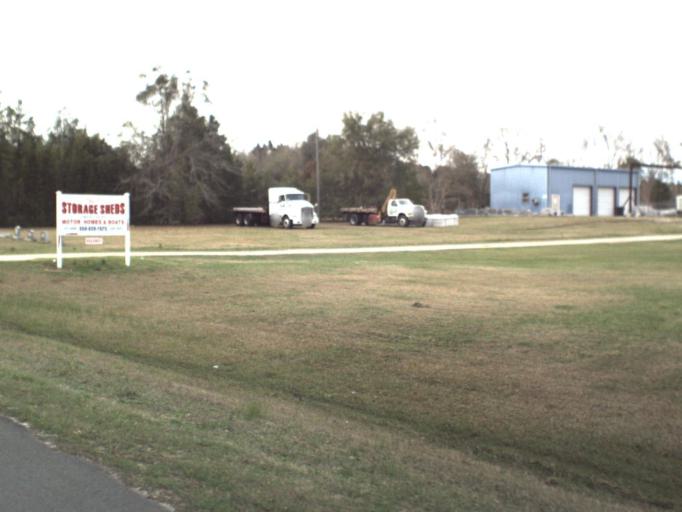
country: US
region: Florida
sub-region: Gulf County
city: Wewahitchka
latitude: 30.1220
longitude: -85.2162
